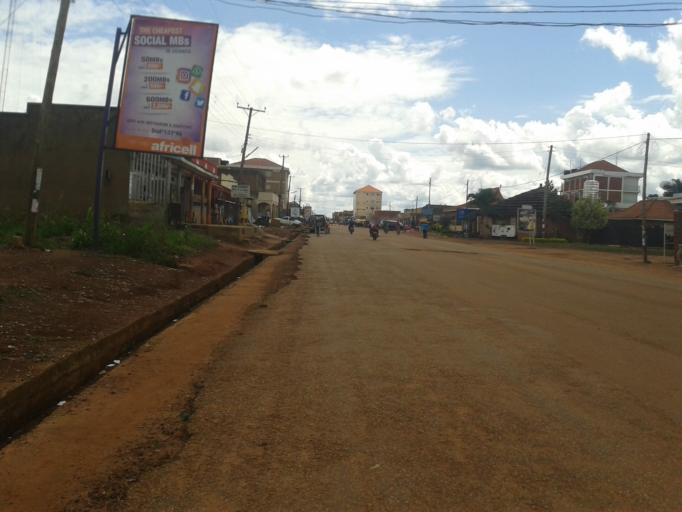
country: UG
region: Northern Region
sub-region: Gulu District
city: Gulu
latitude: 2.7705
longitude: 32.3041
